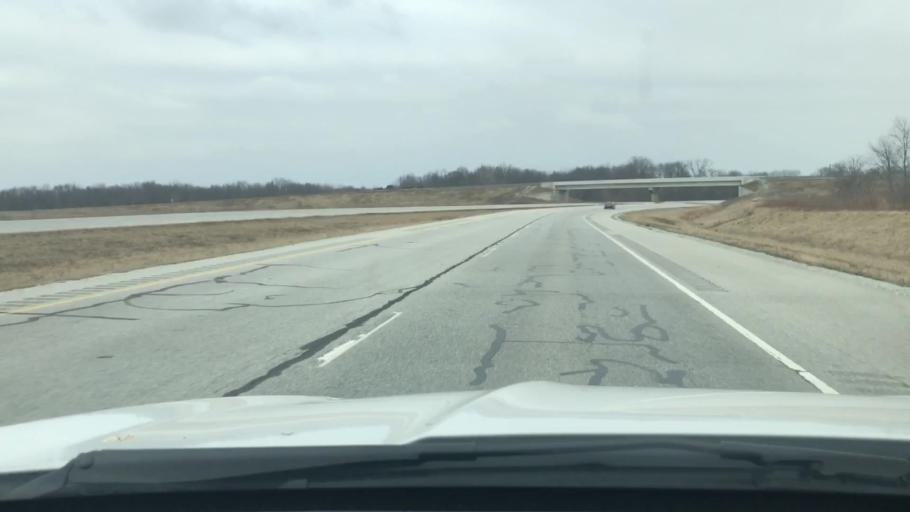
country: US
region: Indiana
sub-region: Carroll County
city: Delphi
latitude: 40.6429
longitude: -86.5799
